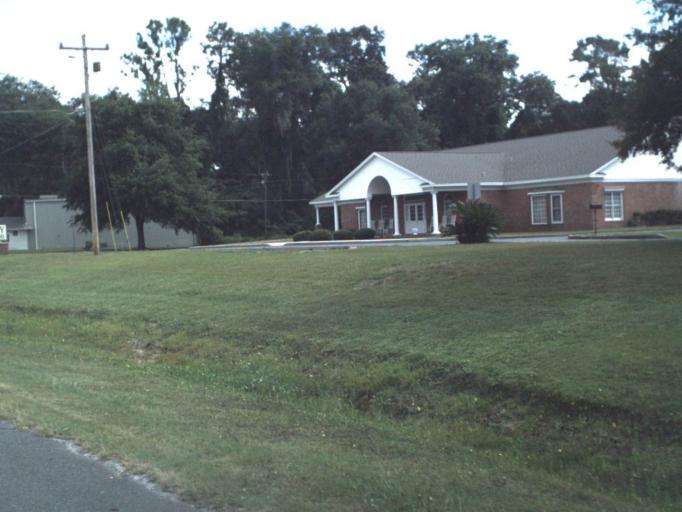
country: US
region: Florida
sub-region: Columbia County
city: Lake City
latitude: 30.1519
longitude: -82.6430
